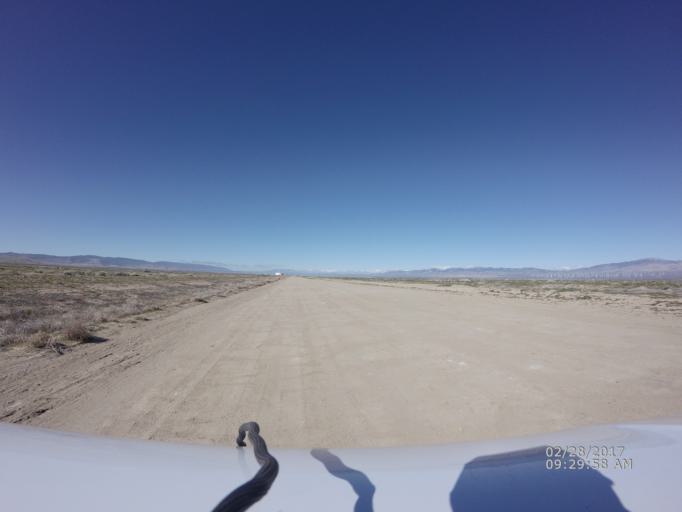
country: US
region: California
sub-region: Los Angeles County
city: Green Valley
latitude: 34.8049
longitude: -118.3514
